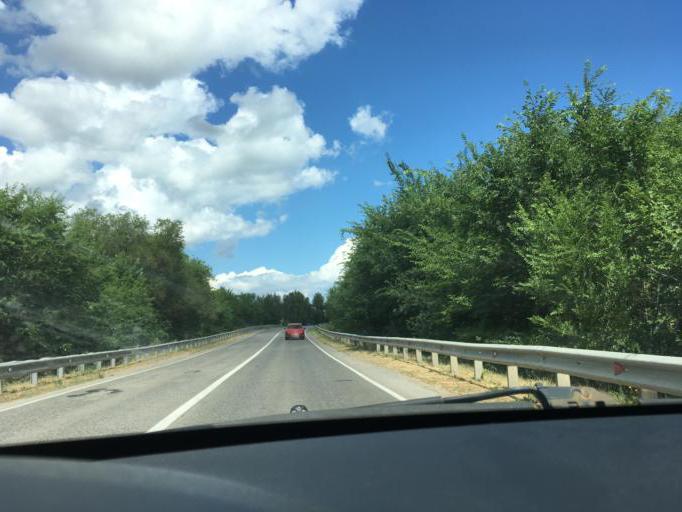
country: RU
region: Samara
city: Bezenchuk
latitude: 53.0385
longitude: 49.4419
